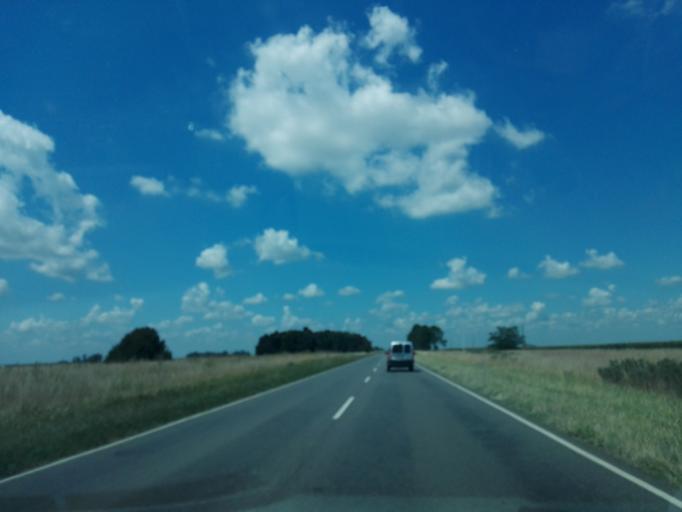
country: AR
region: Buenos Aires
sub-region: Partido de General Belgrano
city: General Belgrano
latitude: -35.9131
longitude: -58.6194
